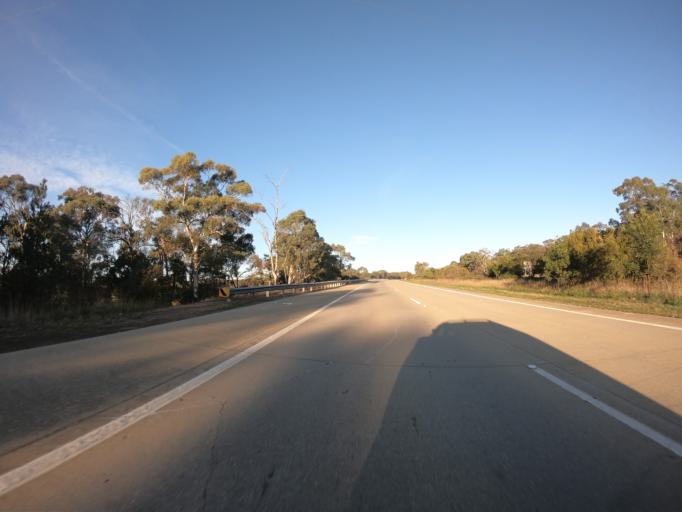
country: AU
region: New South Wales
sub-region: Yass Valley
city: Gundaroo
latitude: -35.1585
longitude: 149.3234
